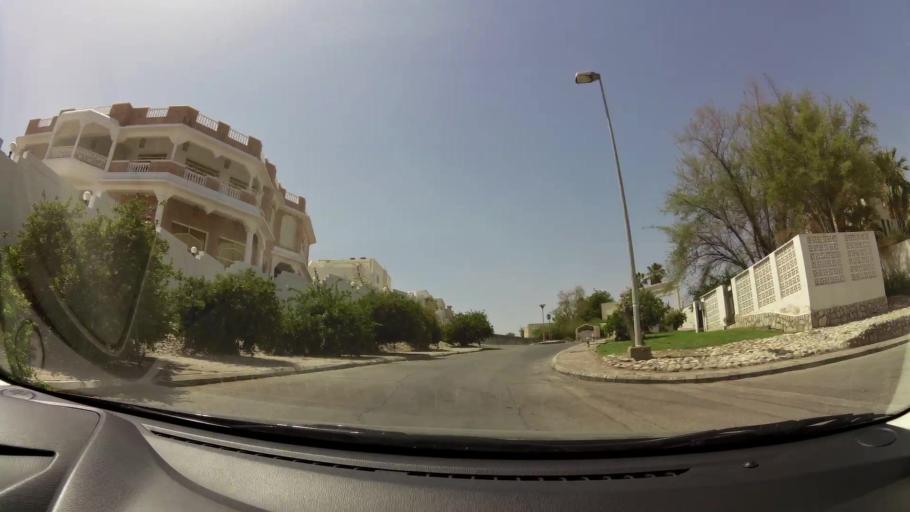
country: OM
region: Muhafazat Masqat
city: Bawshar
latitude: 23.5959
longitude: 58.4545
